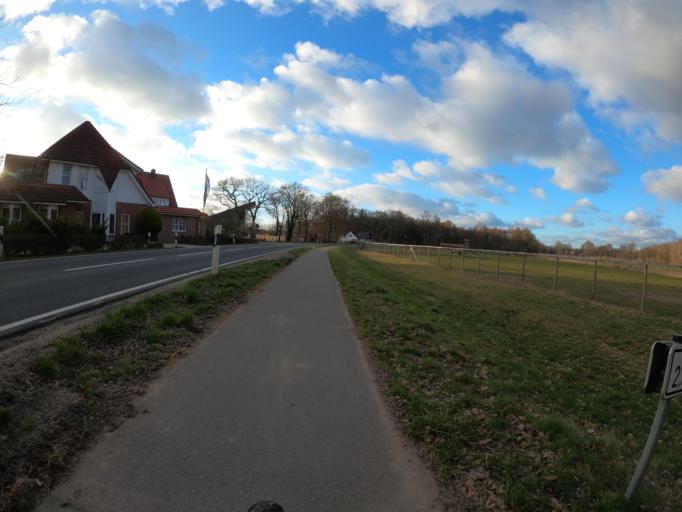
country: DE
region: Lower Saxony
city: Meppen
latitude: 52.6602
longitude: 7.3168
